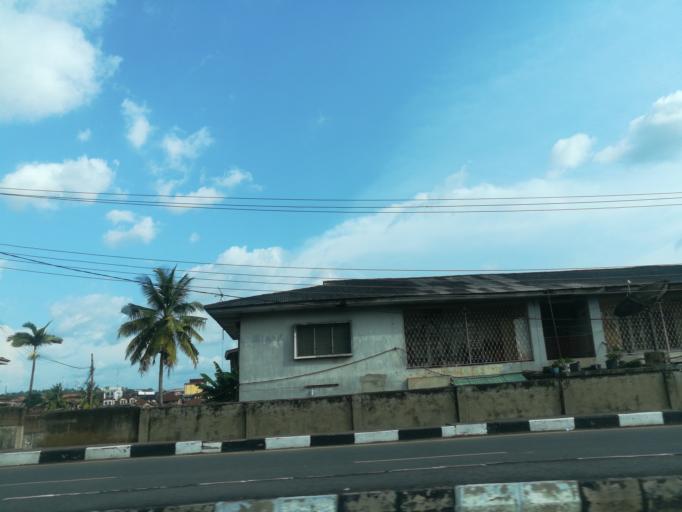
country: NG
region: Oyo
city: Ibadan
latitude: 7.3952
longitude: 3.8813
